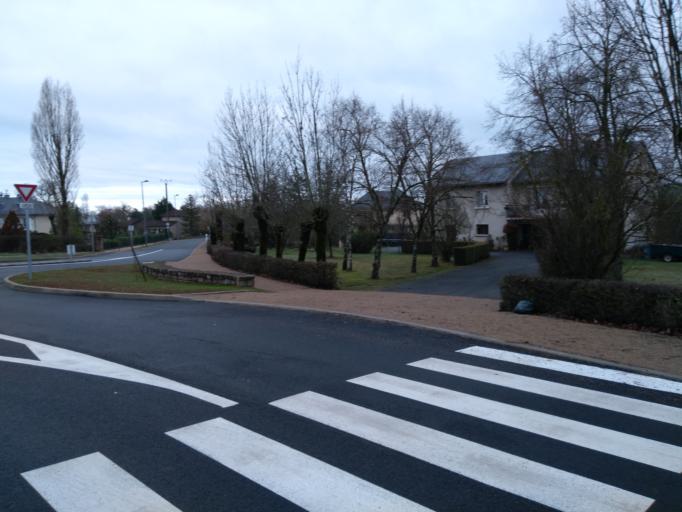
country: FR
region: Midi-Pyrenees
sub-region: Departement de l'Aveyron
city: Sainte-Radegonde
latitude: 44.3431
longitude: 2.6245
